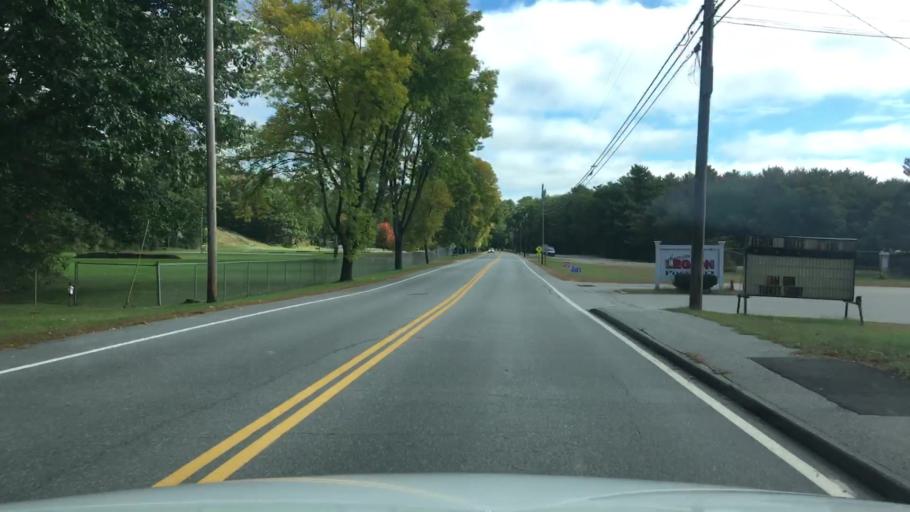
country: US
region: Maine
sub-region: Cumberland County
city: Brunswick
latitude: 43.9235
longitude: -69.9438
